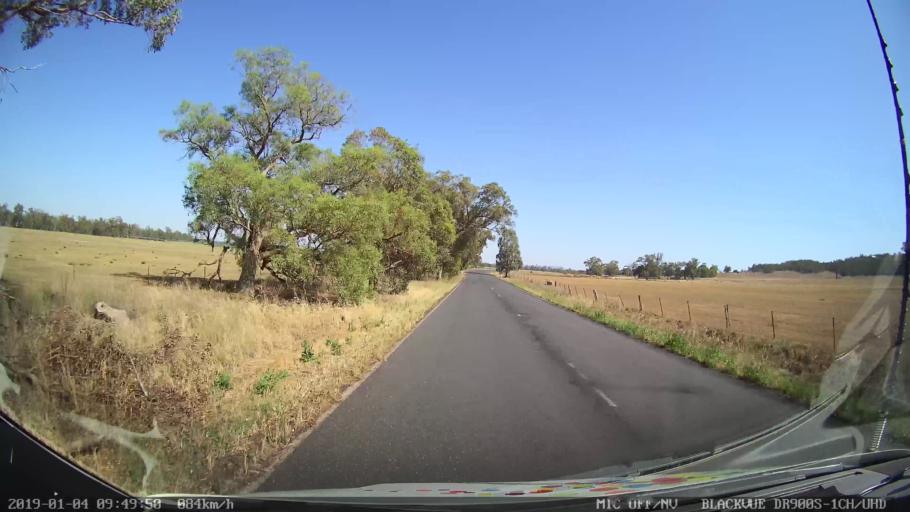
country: AU
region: New South Wales
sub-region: Cabonne
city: Canowindra
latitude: -33.5913
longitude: 148.4159
